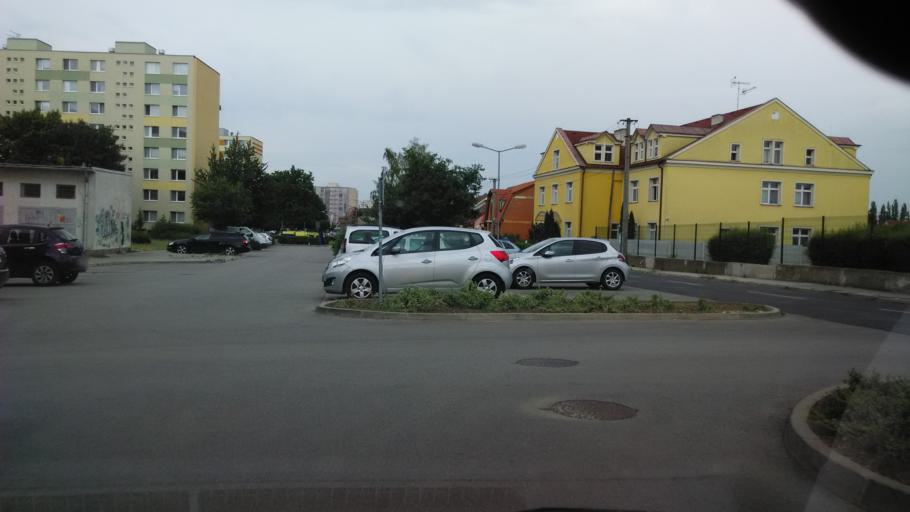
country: SK
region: Trnavsky
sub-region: Okres Trnava
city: Trnava
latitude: 48.3814
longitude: 17.5774
